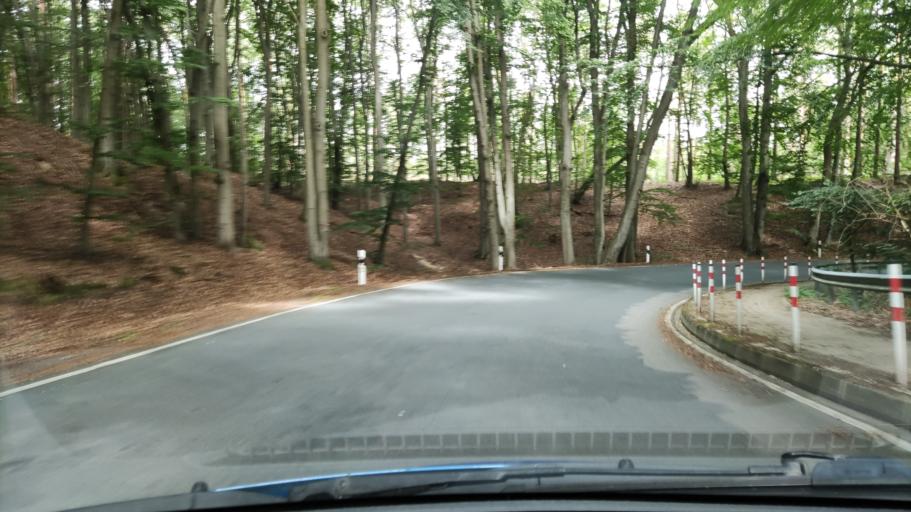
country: DE
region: Lower Saxony
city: Schnega
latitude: 52.9300
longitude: 10.9128
